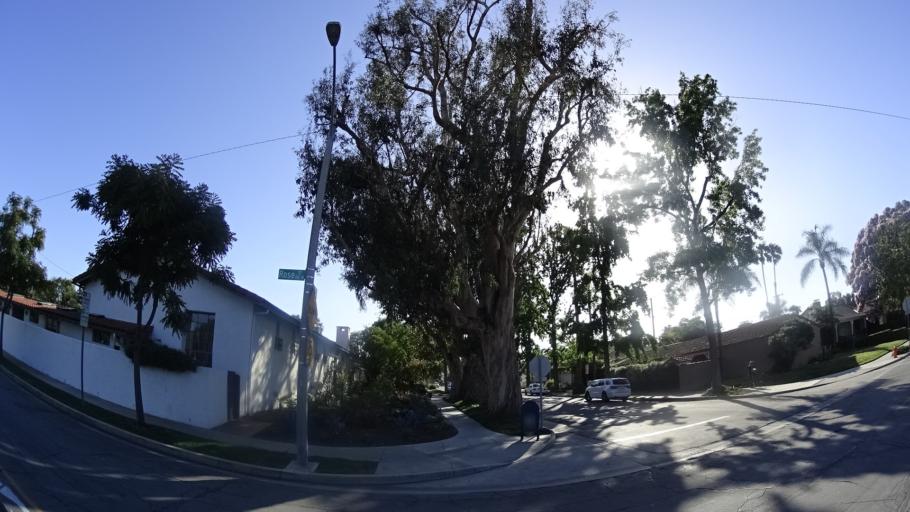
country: US
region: California
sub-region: Los Angeles County
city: Universal City
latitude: 34.1503
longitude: -118.3455
